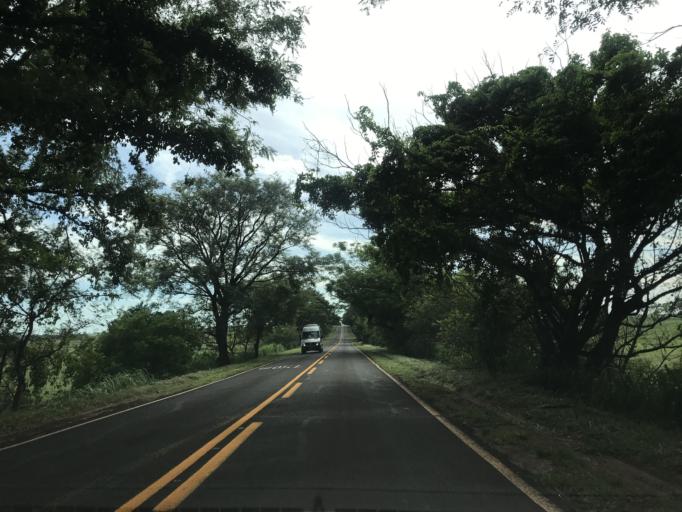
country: BR
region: Parana
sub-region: Terra Rica
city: Terra Rica
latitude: -22.7749
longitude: -52.6529
